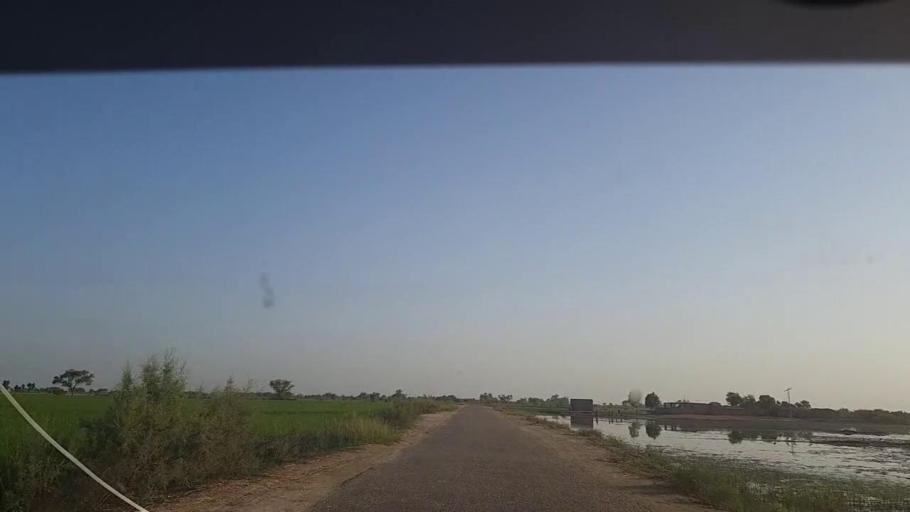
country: PK
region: Sindh
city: Thul
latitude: 28.1941
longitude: 68.8729
